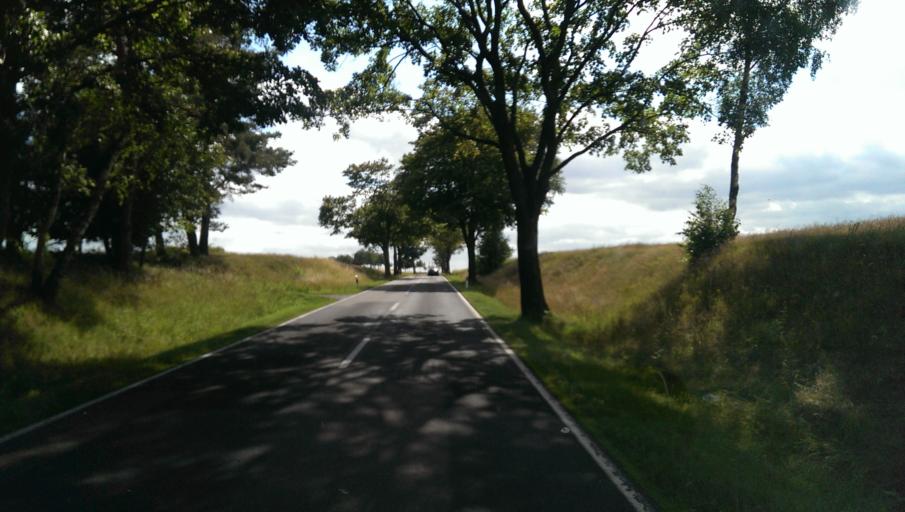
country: DE
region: Saxony-Anhalt
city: Nudersdorf
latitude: 52.0102
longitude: 12.6001
